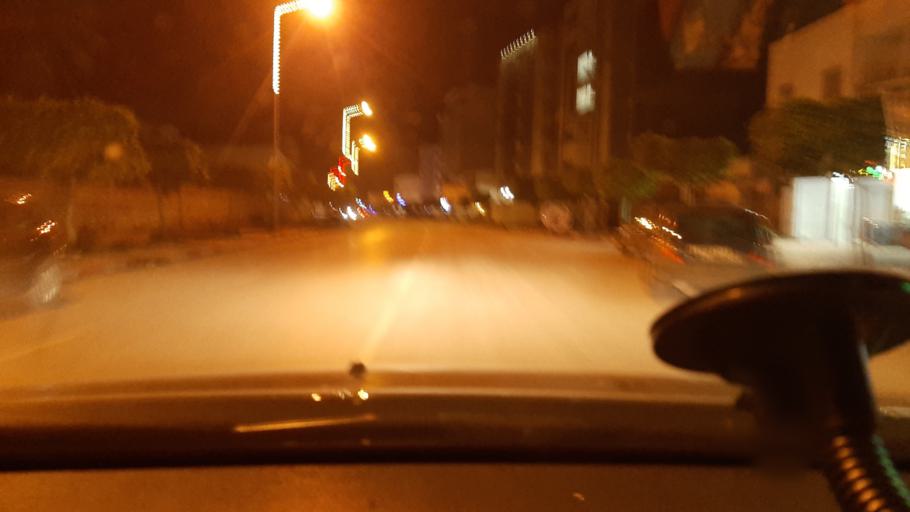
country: TN
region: Safaqis
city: Sfax
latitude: 34.7821
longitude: 10.7230
